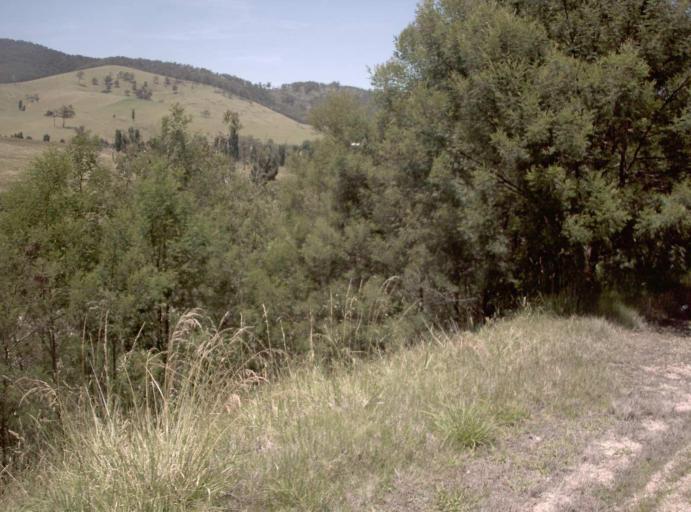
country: AU
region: Victoria
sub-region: East Gippsland
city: Bairnsdale
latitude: -37.5056
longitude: 147.8402
